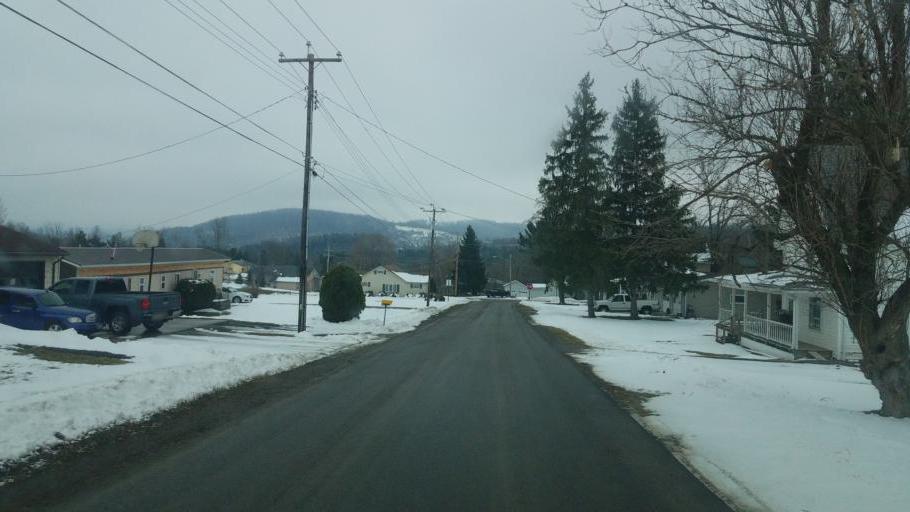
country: US
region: Pennsylvania
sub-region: Tioga County
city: Westfield
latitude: 42.0424
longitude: -77.5447
